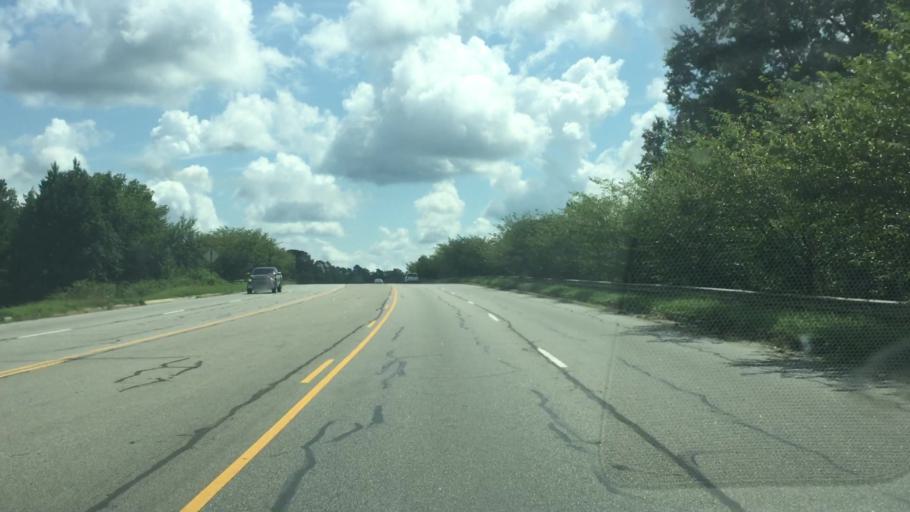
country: US
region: North Carolina
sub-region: Anson County
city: Wadesboro
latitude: 34.9632
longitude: -80.0519
